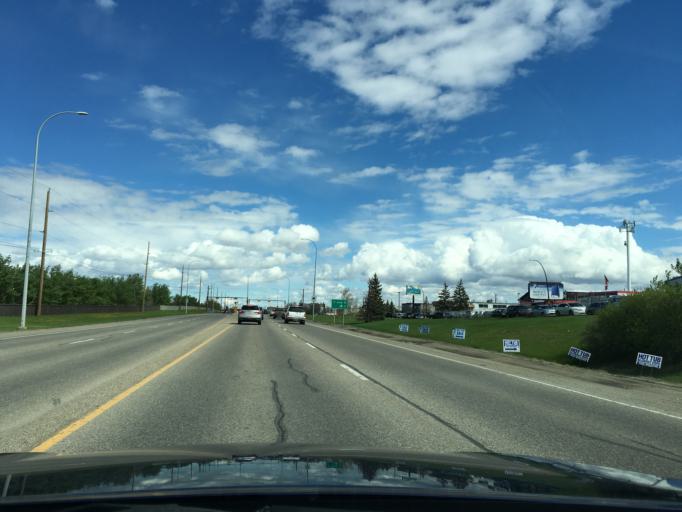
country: CA
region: Alberta
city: Calgary
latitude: 51.0562
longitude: -114.0017
